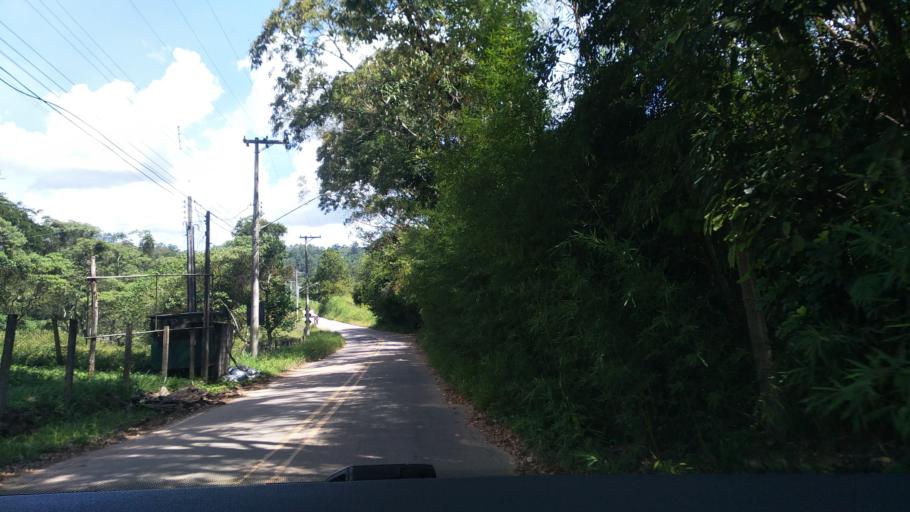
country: BR
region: Sao Paulo
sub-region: Varzea Paulista
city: Varzea Paulista
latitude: -23.2687
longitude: -46.8822
